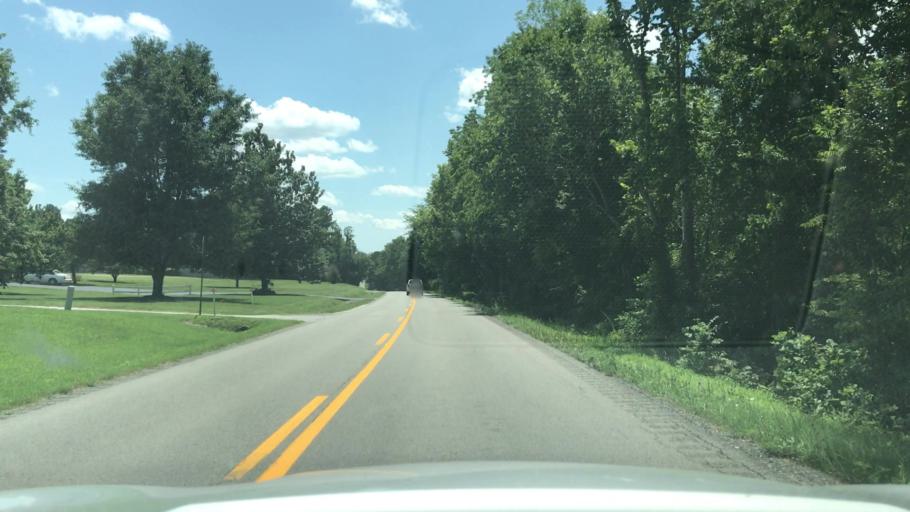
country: US
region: Kentucky
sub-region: Christian County
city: Hopkinsville
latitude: 36.9129
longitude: -87.4422
